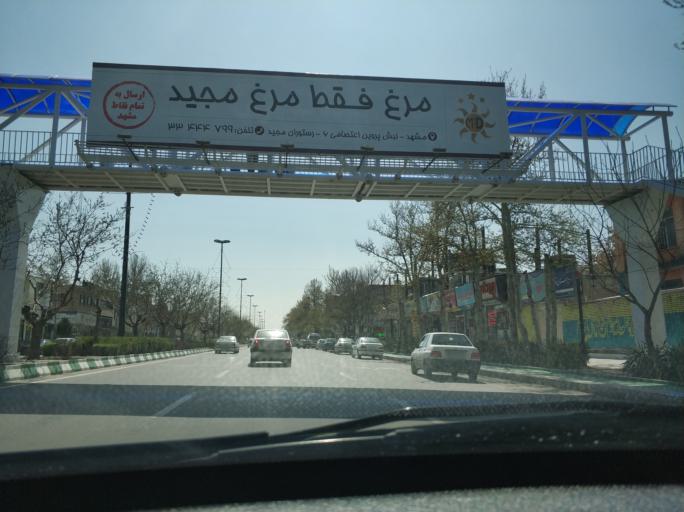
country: IR
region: Razavi Khorasan
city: Mashhad
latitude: 36.2607
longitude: 59.6060
